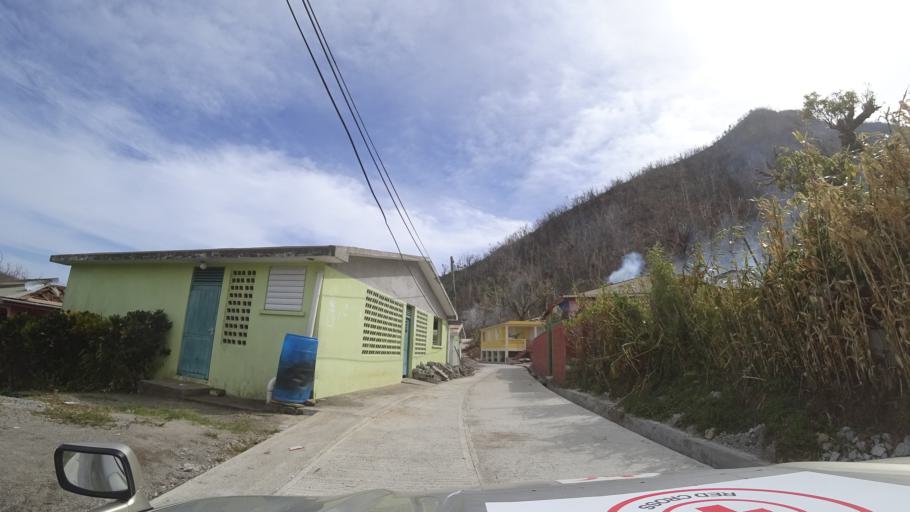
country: DM
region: Saint Patrick
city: Berekua
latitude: 15.2357
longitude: -61.3339
